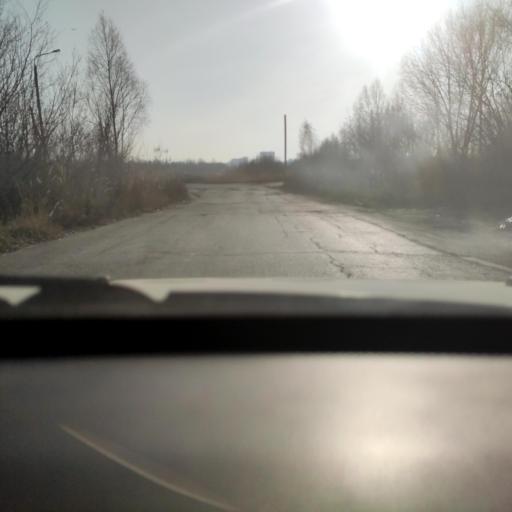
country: RU
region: Perm
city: Perm
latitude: 58.0353
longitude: 56.1911
